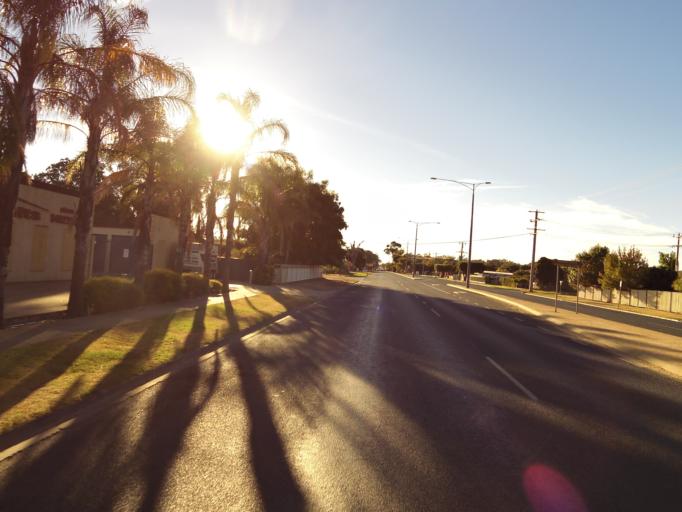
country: AU
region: Victoria
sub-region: Campaspe
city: Echuca
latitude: -36.1404
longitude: 144.7340
